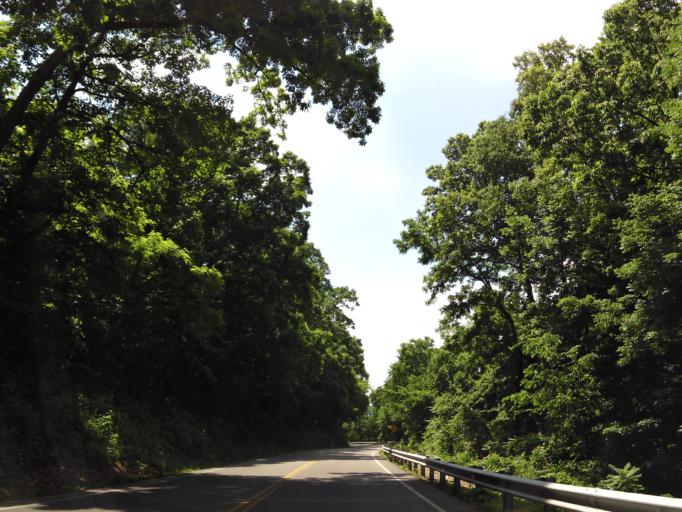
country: US
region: Tennessee
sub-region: Bledsoe County
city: Pikeville
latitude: 35.5937
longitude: -85.1484
